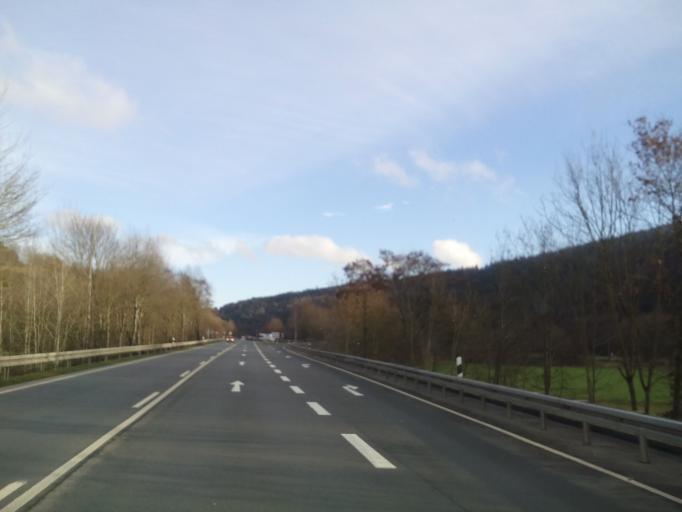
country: DE
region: Bavaria
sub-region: Upper Franconia
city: Kulmbach
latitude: 50.1131
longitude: 11.4797
